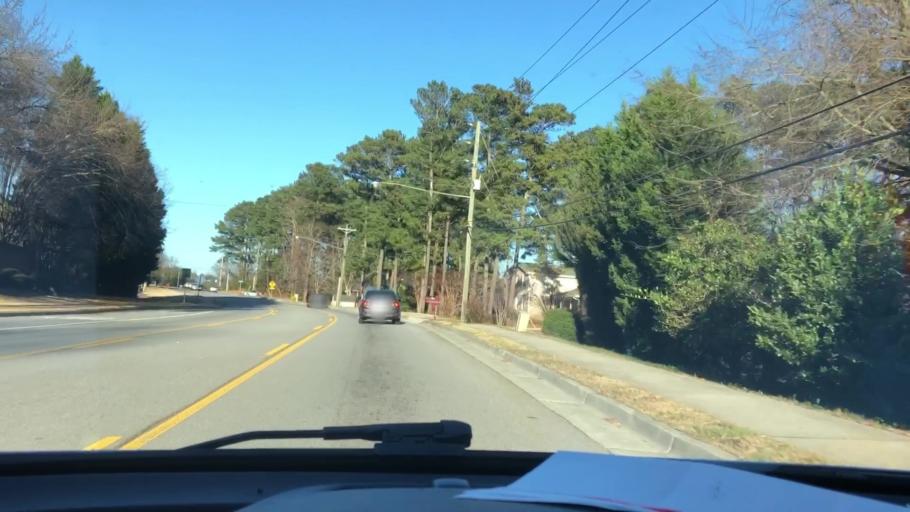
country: US
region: Georgia
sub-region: Gwinnett County
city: Snellville
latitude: 33.8975
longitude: -84.0515
